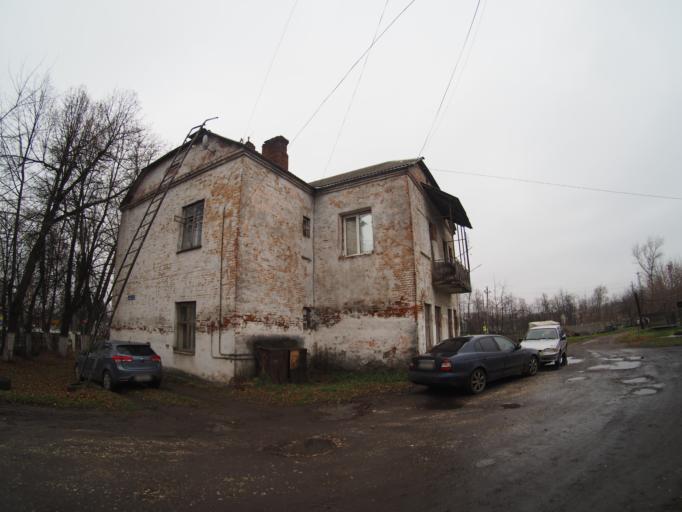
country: RU
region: Moskovskaya
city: Mikhnevo
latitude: 55.1191
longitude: 37.9479
